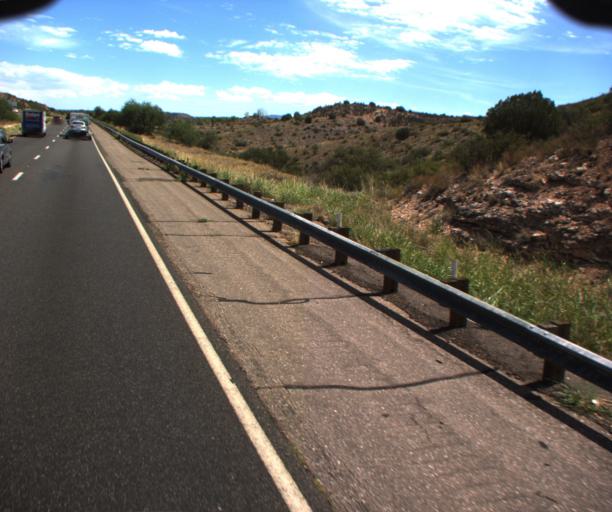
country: US
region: Arizona
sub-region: Yavapai County
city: Lake Montezuma
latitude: 34.6444
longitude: -111.8064
